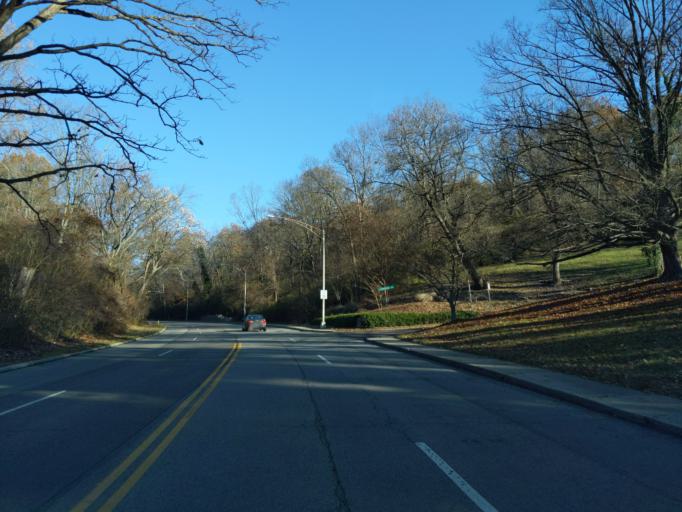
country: US
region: Kentucky
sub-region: Campbell County
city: Dayton
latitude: 39.1263
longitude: -84.4635
